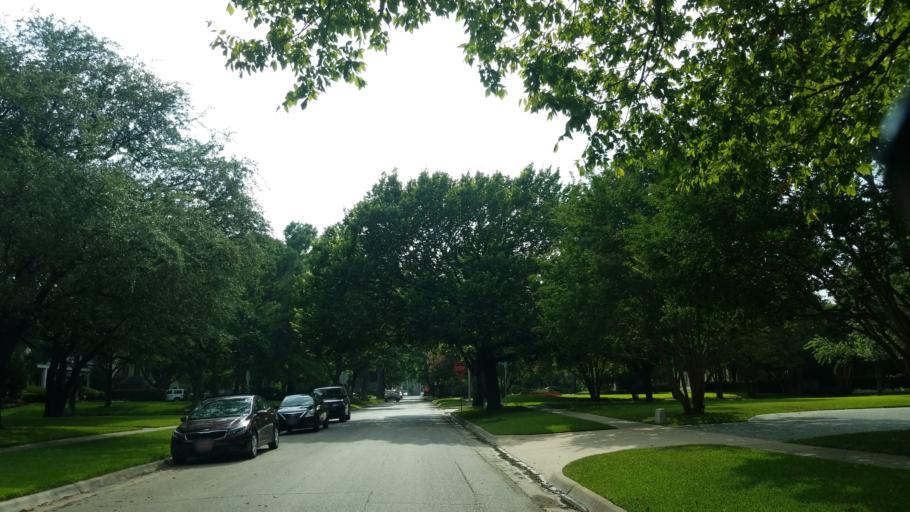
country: US
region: Texas
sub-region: Dallas County
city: University Park
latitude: 32.8468
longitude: -96.8015
